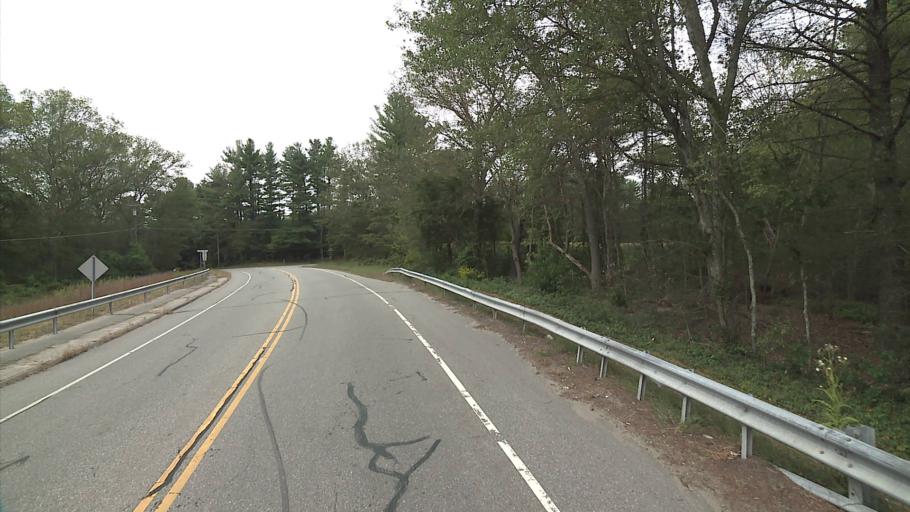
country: US
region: Connecticut
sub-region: Windham County
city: Plainfield Village
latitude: 41.6508
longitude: -71.9640
